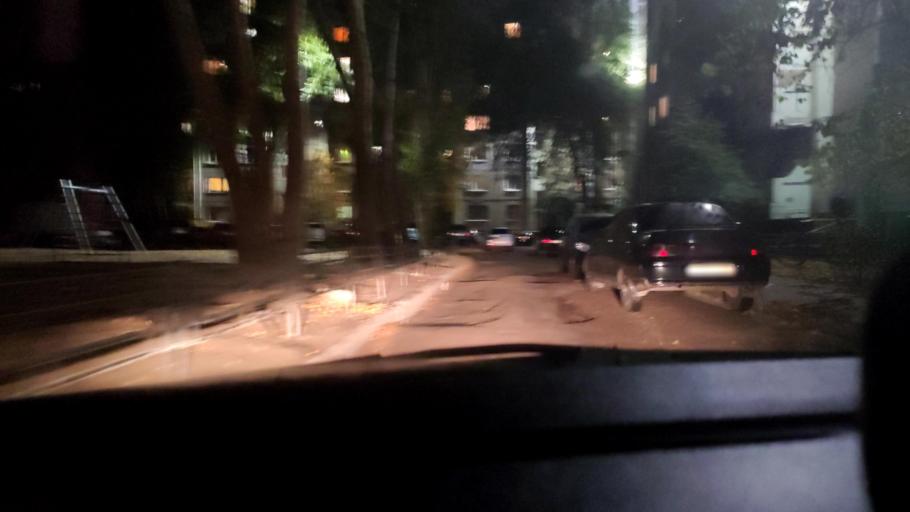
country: RU
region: Voronezj
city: Podgornoye
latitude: 51.6994
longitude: 39.1369
